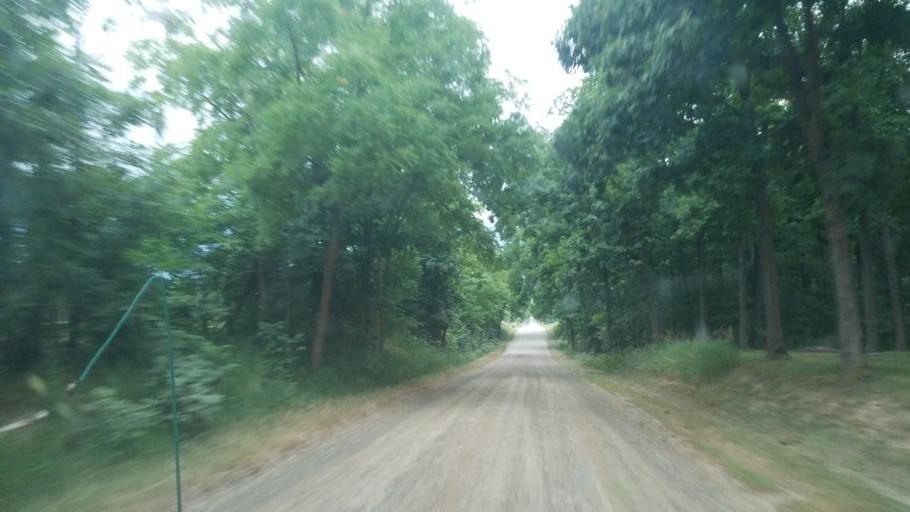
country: US
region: Ohio
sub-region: Defiance County
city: Hicksville
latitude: 41.3289
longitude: -84.8157
